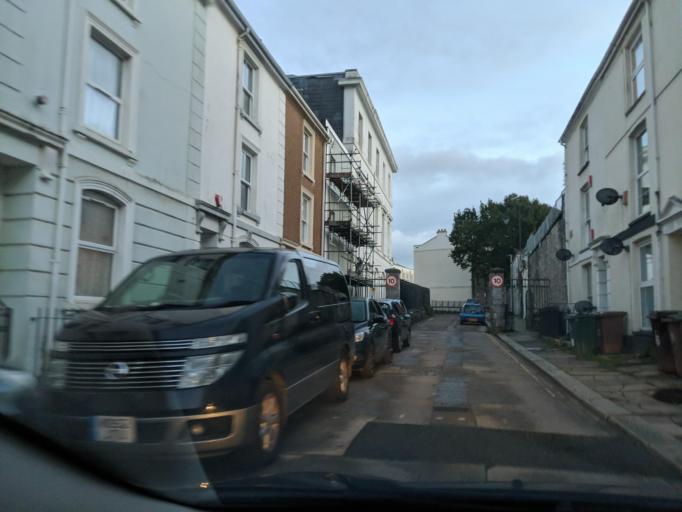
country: GB
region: England
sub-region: Cornwall
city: Millbrook
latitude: 50.3679
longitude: -4.1719
